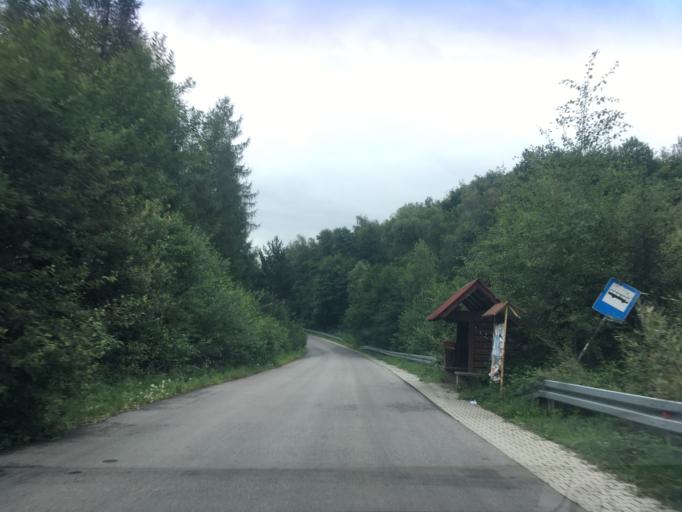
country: PL
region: Lesser Poland Voivodeship
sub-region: Powiat myslenicki
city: Trzemesnia
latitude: 49.8533
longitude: 20.0224
